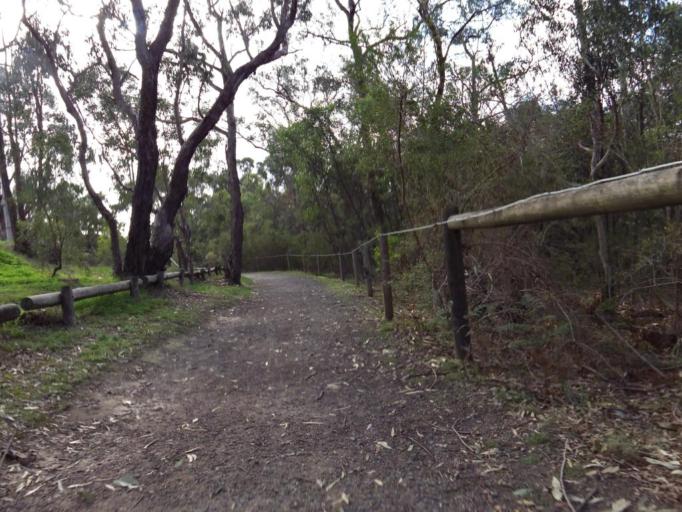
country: AU
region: Victoria
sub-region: Manningham
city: Park Orchards
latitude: -37.7765
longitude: 145.2200
